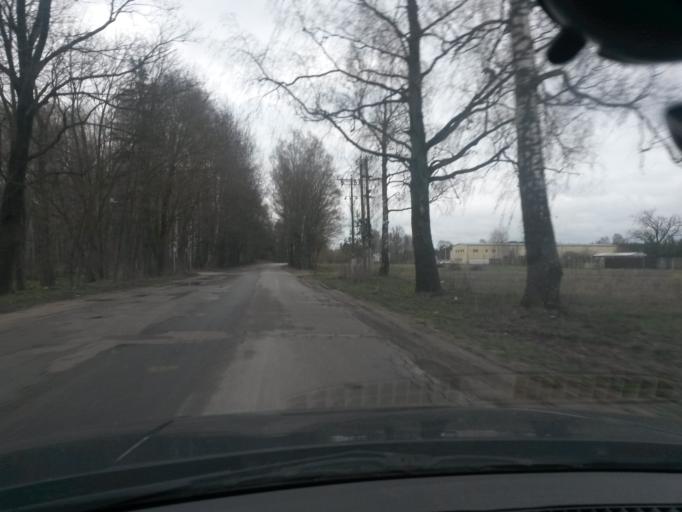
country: LV
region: Kekava
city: Kekava
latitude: 56.8925
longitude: 24.2418
